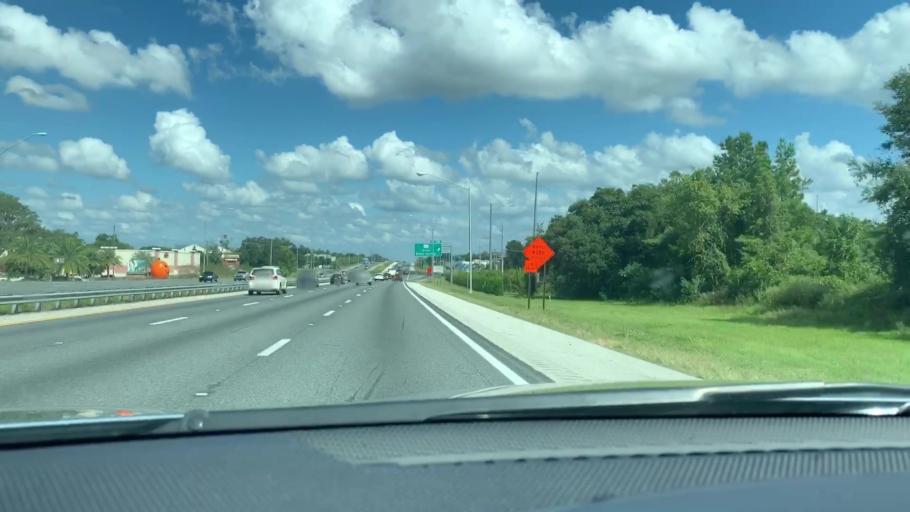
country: US
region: Florida
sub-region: Marion County
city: Ocala
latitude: 29.1435
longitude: -82.1864
